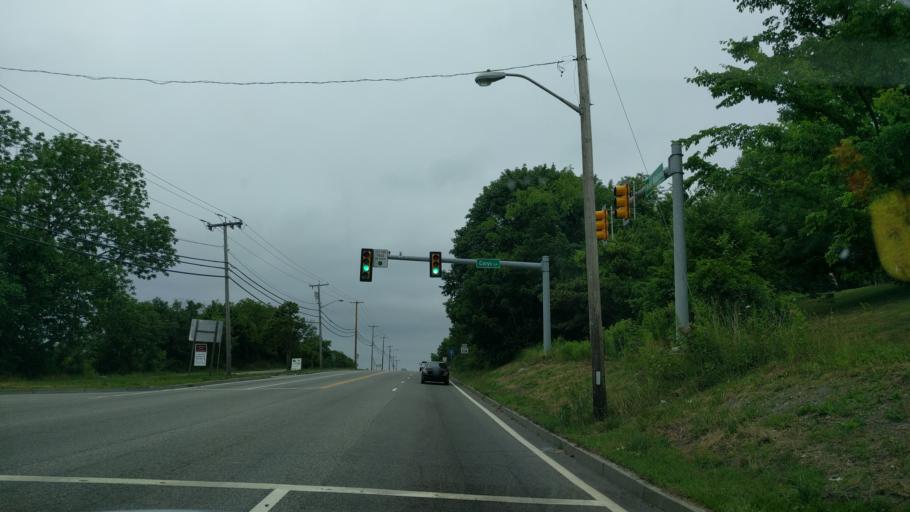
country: US
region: Rhode Island
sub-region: Newport County
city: Portsmouth
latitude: 41.5944
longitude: -71.2645
